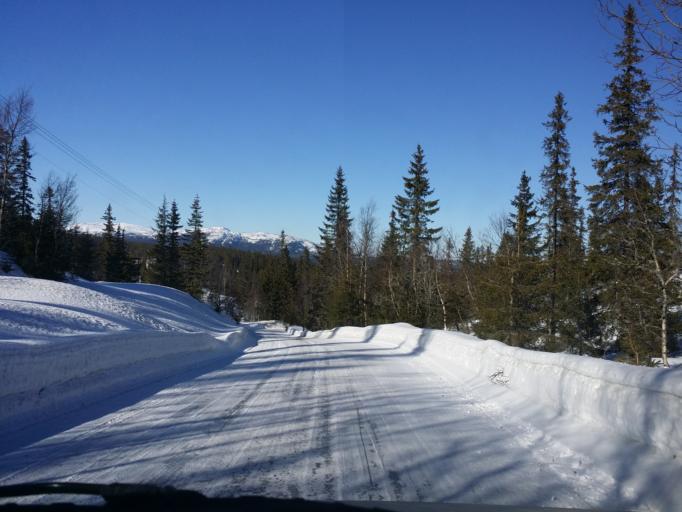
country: NO
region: Buskerud
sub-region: Ringerike
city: Honefoss
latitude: 60.3964
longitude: 10.0083
